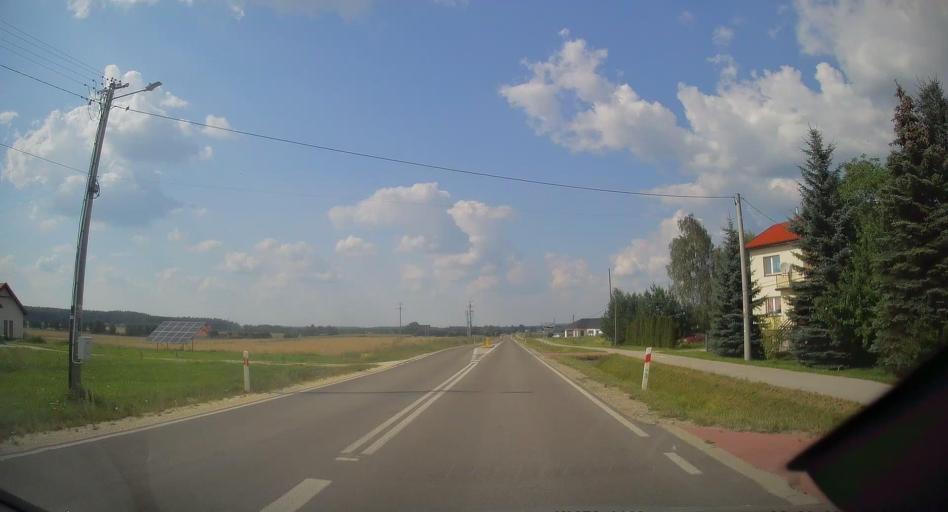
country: PL
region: Swietokrzyskie
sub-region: Powiat kielecki
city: Lopuszno
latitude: 50.9552
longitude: 20.2505
